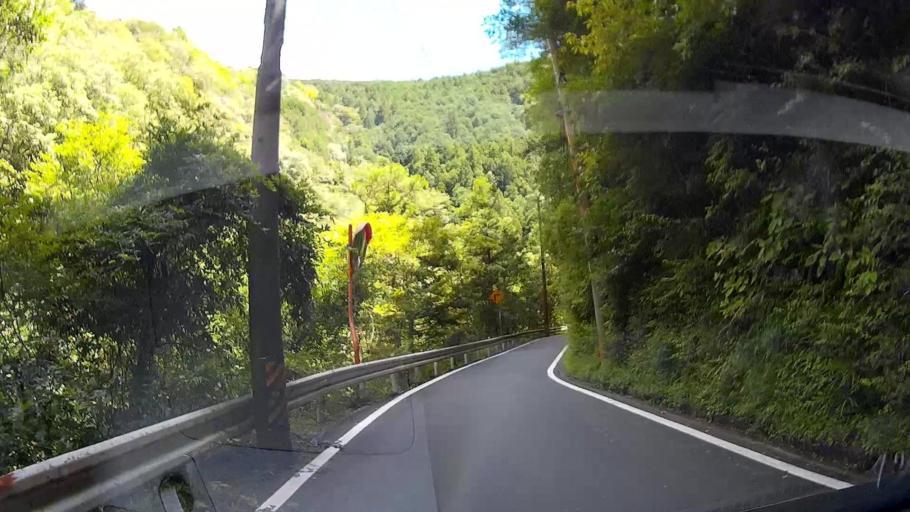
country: JP
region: Shizuoka
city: Shizuoka-shi
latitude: 35.1743
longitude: 138.3049
